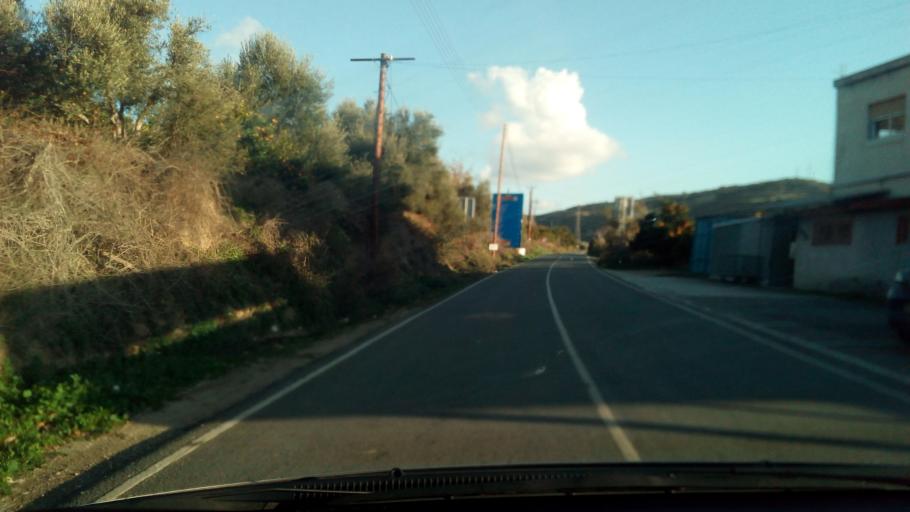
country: CY
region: Pafos
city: Polis
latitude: 34.9840
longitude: 32.4531
